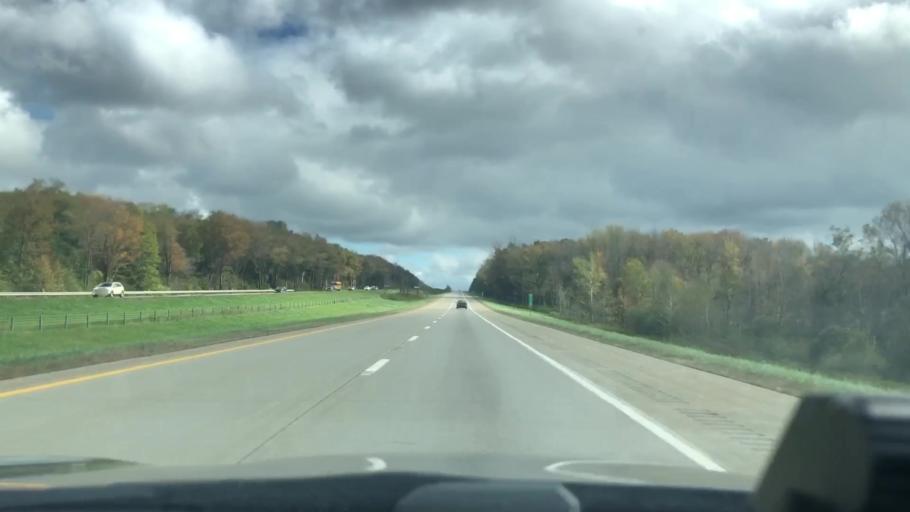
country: US
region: Pennsylvania
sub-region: Monroe County
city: Pocono Pines
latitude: 41.2185
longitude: -75.4796
